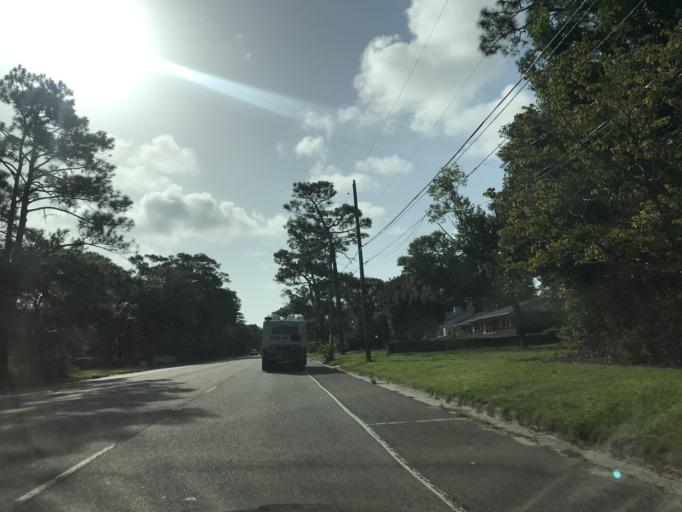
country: US
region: North Carolina
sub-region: New Hanover County
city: Wilmington
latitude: 34.2233
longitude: -77.9199
